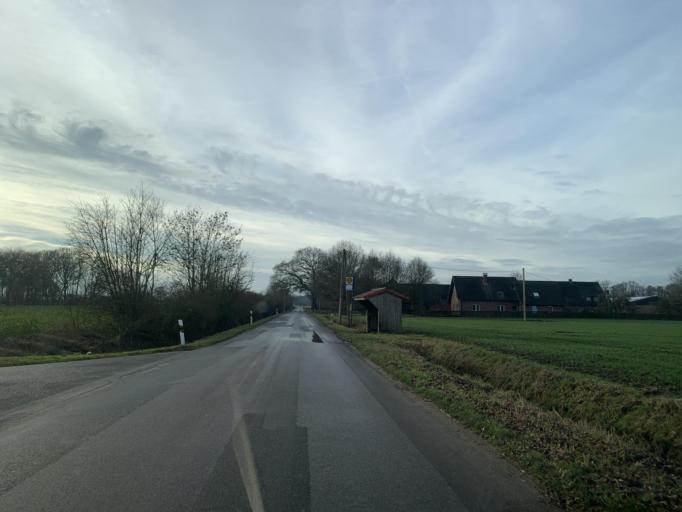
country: DE
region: North Rhine-Westphalia
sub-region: Regierungsbezirk Munster
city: Dulmen
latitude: 51.8320
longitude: 7.3433
